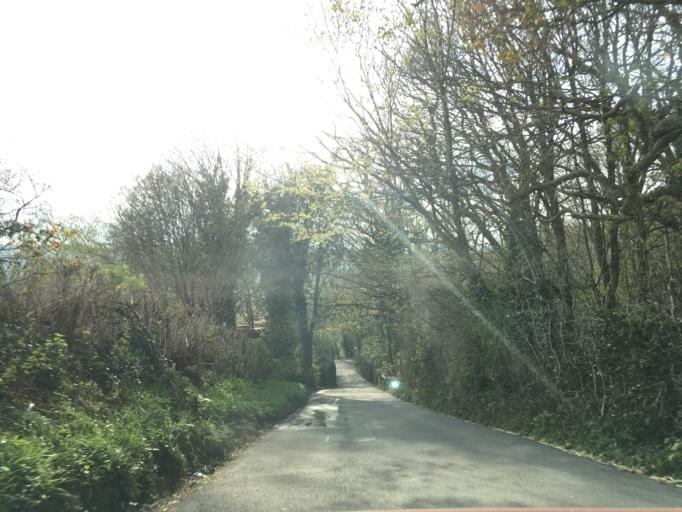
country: GB
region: Wales
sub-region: Caerphilly County Borough
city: Maesycwmmer
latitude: 51.6320
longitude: -3.2258
